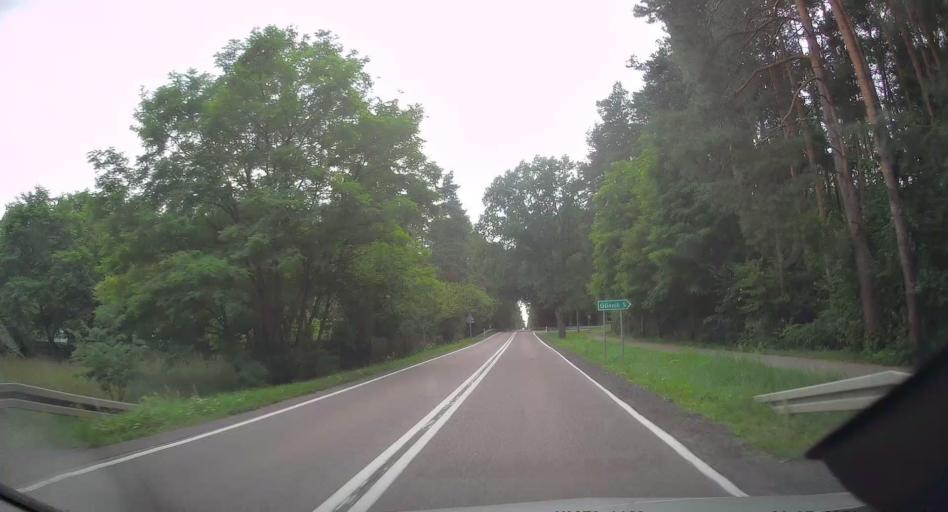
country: PL
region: Lodz Voivodeship
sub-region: Powiat tomaszowski
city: Lubochnia
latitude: 51.5457
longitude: 20.0917
